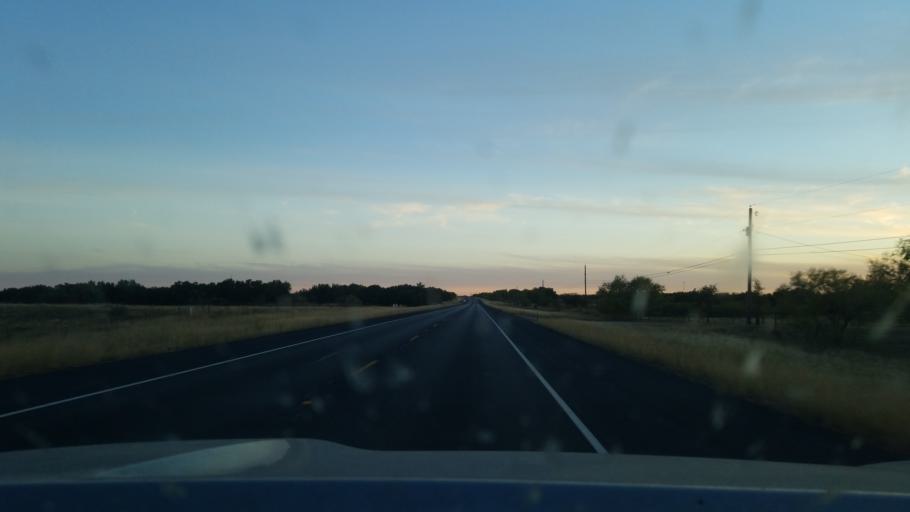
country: US
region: Texas
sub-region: Stephens County
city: Breckenridge
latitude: 32.6536
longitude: -98.9027
